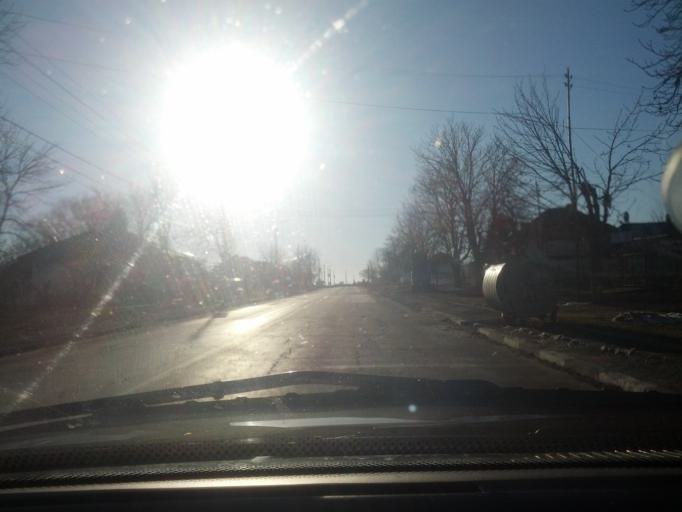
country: BG
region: Vratsa
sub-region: Obshtina Miziya
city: Miziya
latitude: 43.7045
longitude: 23.8262
